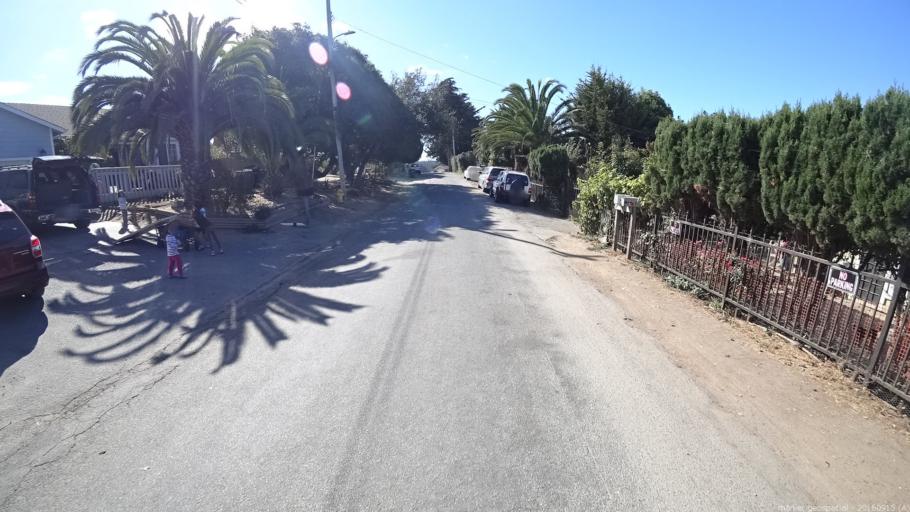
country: US
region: California
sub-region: Monterey County
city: Las Lomas
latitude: 36.8713
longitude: -121.7345
